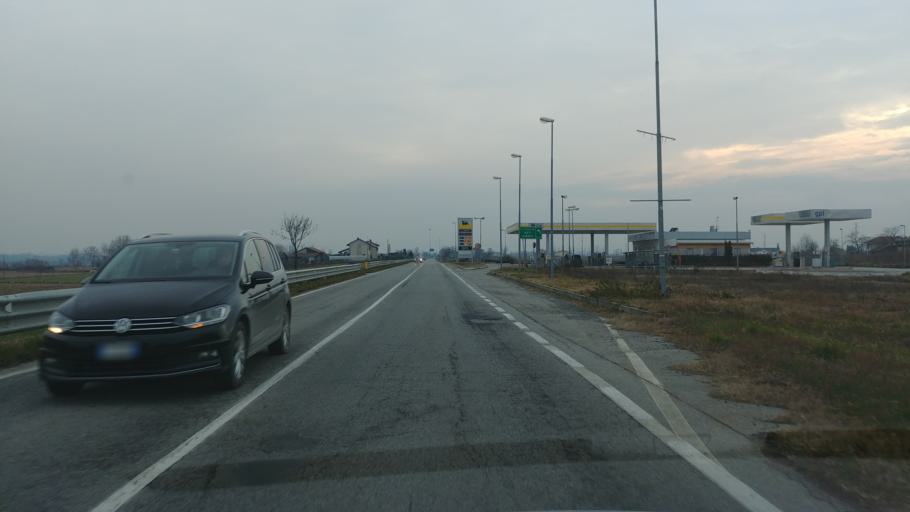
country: IT
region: Piedmont
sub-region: Provincia di Cuneo
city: Castelletto Stura
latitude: 44.4648
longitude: 7.6327
